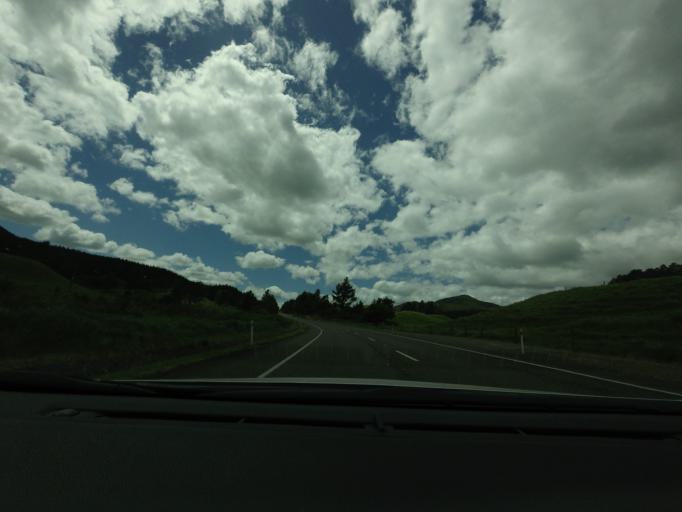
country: NZ
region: Bay of Plenty
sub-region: Rotorua District
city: Rotorua
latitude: -38.3336
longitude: 176.3674
